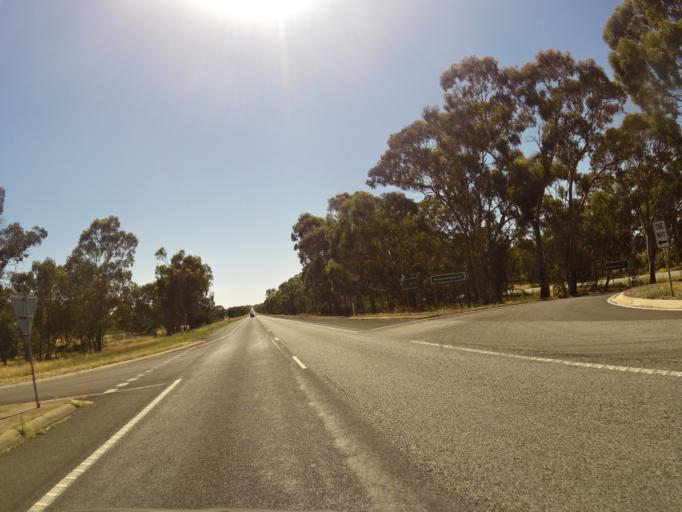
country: AU
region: Victoria
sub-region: Greater Shepparton
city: Shepparton
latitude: -36.8491
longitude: 145.3397
